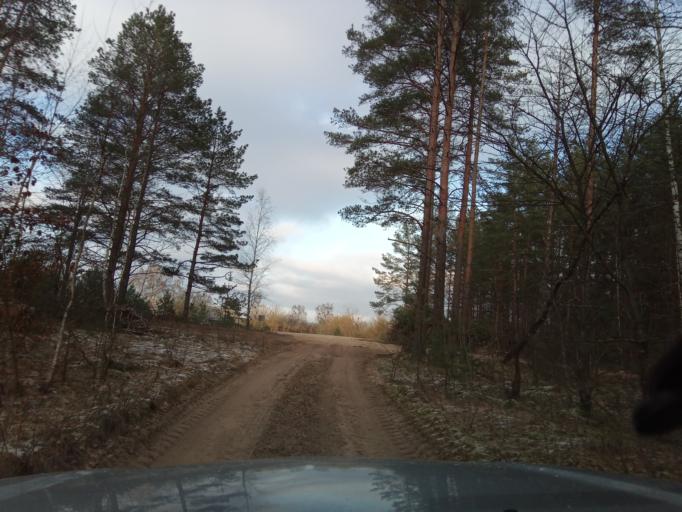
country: LT
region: Alytaus apskritis
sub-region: Alytaus rajonas
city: Daugai
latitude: 54.1109
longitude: 24.3026
